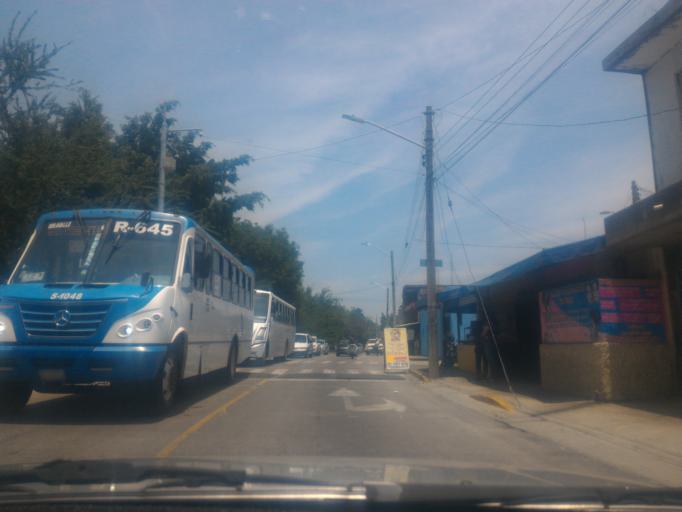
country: MX
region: Jalisco
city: Guadalajara
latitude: 20.6206
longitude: -103.3695
